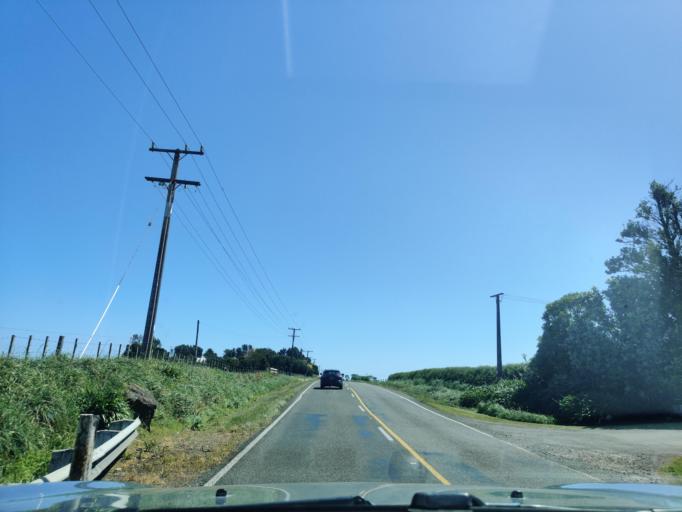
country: NZ
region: Taranaki
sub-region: South Taranaki District
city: Hawera
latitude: -39.5490
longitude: 174.1062
